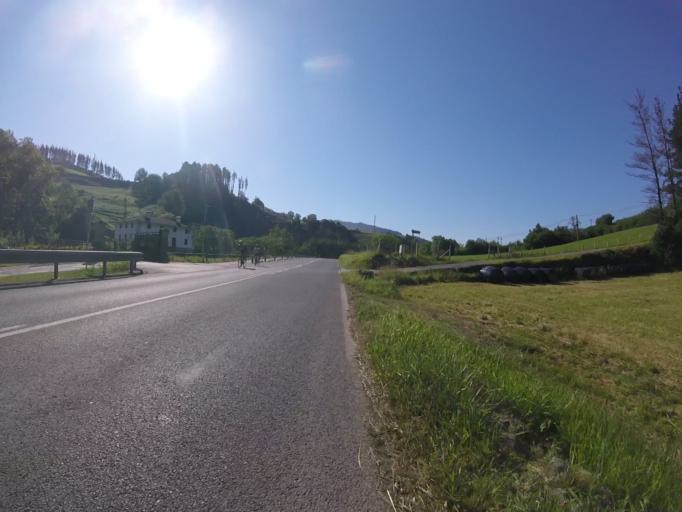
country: ES
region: Basque Country
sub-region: Provincia de Guipuzcoa
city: Azpeitia
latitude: 43.1690
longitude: -2.2512
